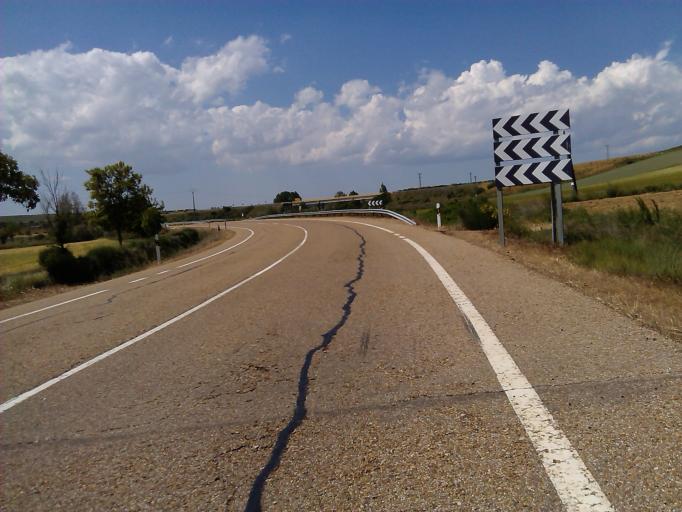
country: ES
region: Castille and Leon
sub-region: Provincia de Palencia
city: Ledigos
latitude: 42.3623
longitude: -4.8663
